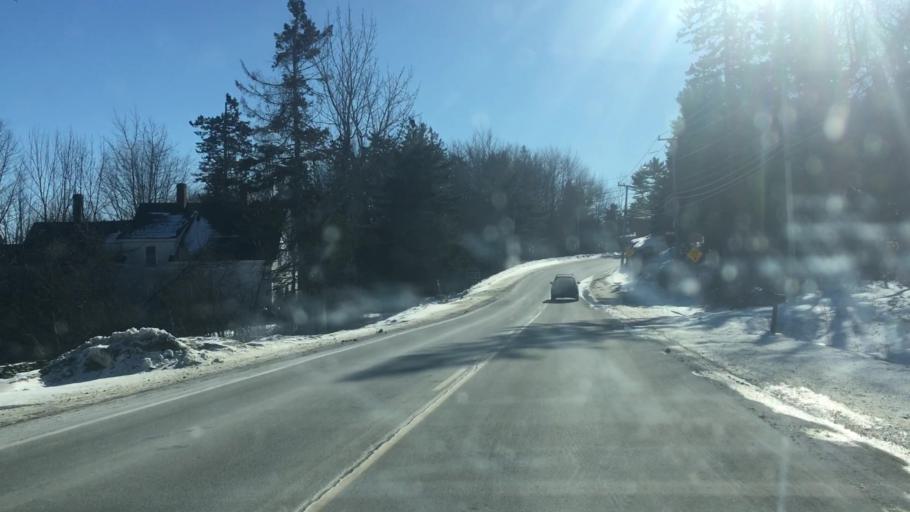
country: US
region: Maine
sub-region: Hancock County
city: Ellsworth
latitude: 44.5213
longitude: -68.4310
